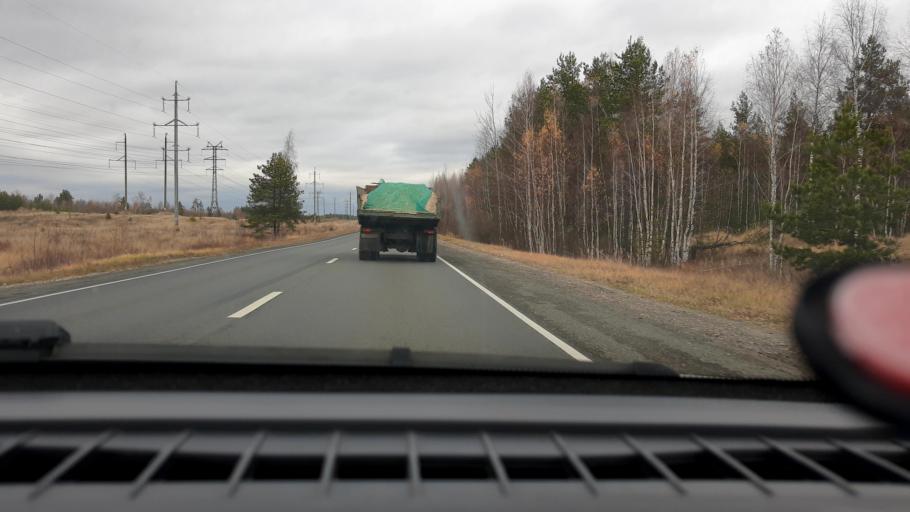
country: RU
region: Nizjnij Novgorod
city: Lukino
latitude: 56.3733
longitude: 43.6226
